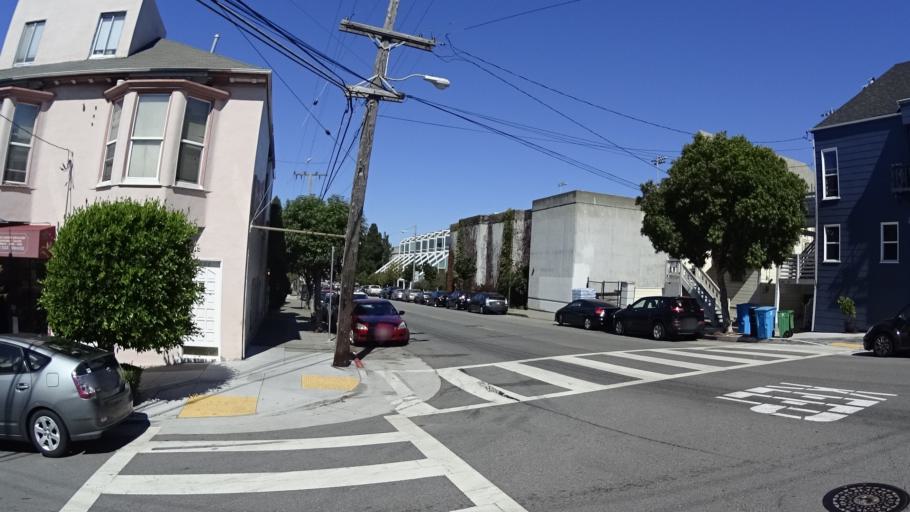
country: US
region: California
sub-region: San Francisco County
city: San Francisco
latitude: 37.7757
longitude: -122.4550
